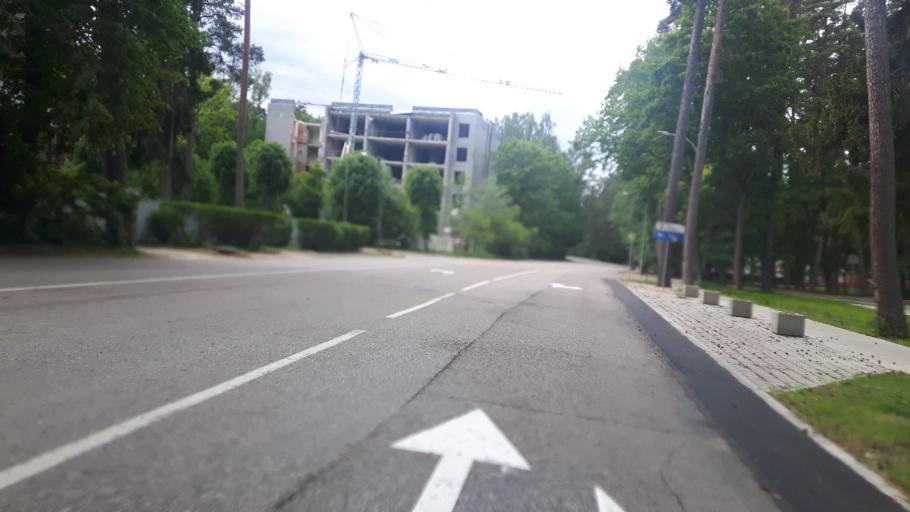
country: LV
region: Jurmala
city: Jurmala
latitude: 56.9773
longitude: 23.8276
